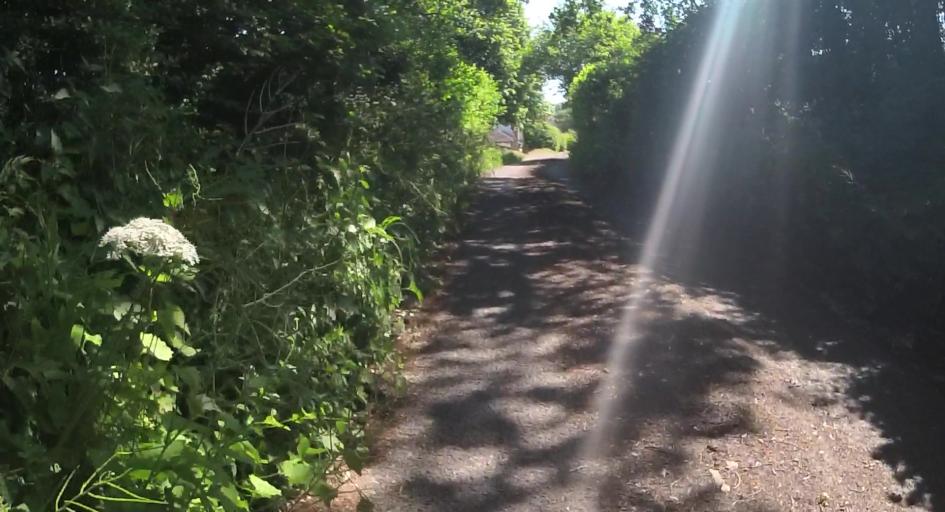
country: GB
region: England
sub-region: Hampshire
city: Kingsclere
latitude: 51.3568
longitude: -1.2759
